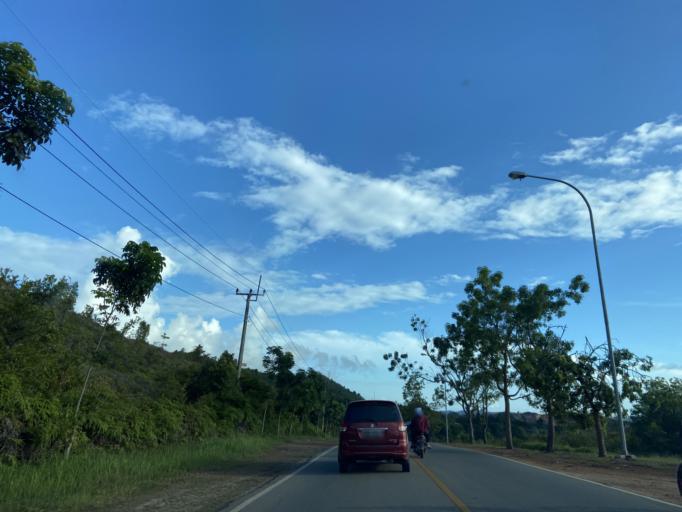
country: SG
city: Singapore
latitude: 0.9903
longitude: 104.0357
